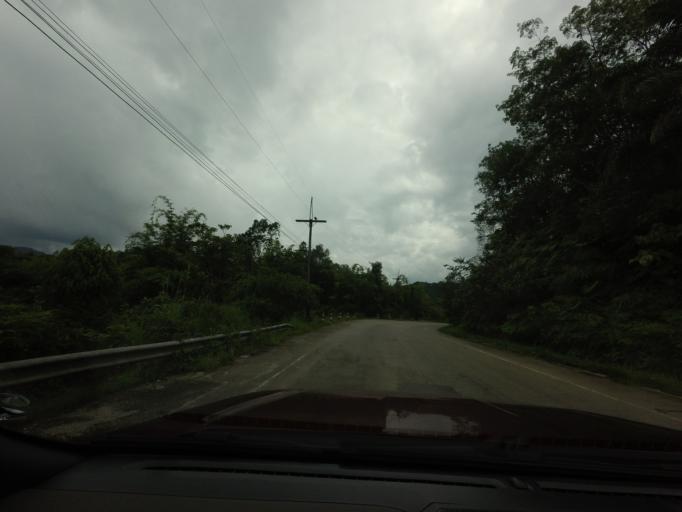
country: TH
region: Narathiwat
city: Sukhirin
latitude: 5.9797
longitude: 101.6970
